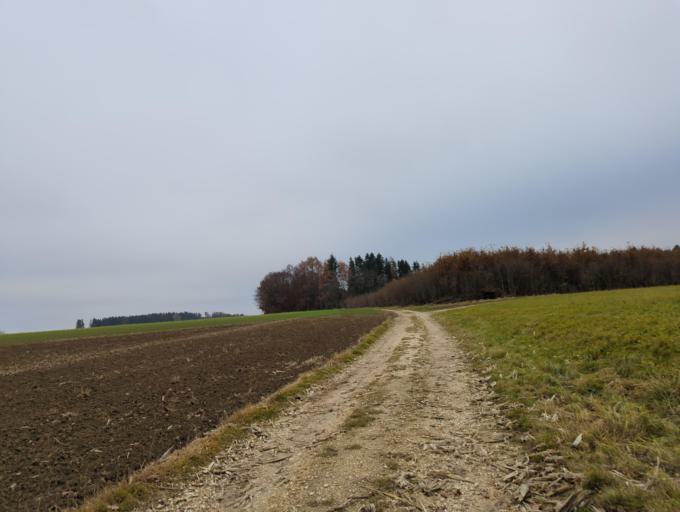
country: DE
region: Bavaria
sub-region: Swabia
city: Rettenbach
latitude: 48.4349
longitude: 10.3213
